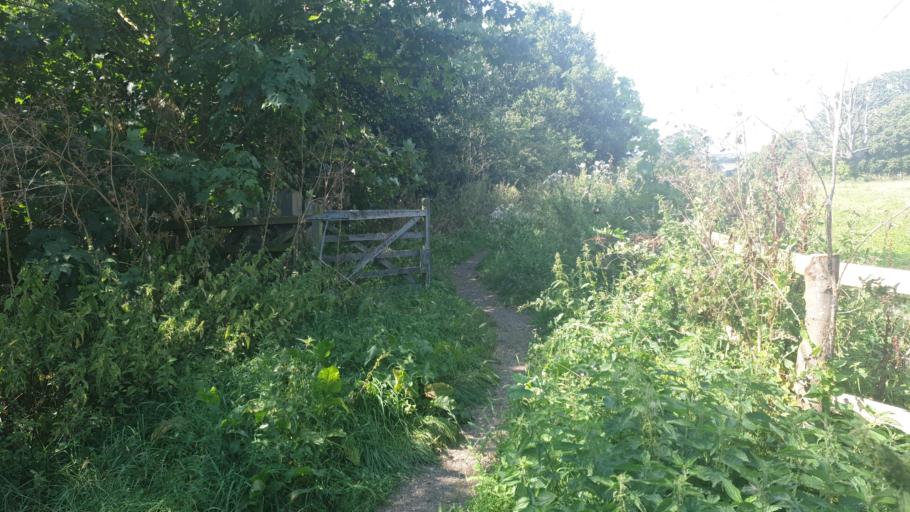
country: GB
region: England
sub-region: Suffolk
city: Shotley Gate
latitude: 51.9285
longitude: 1.2257
